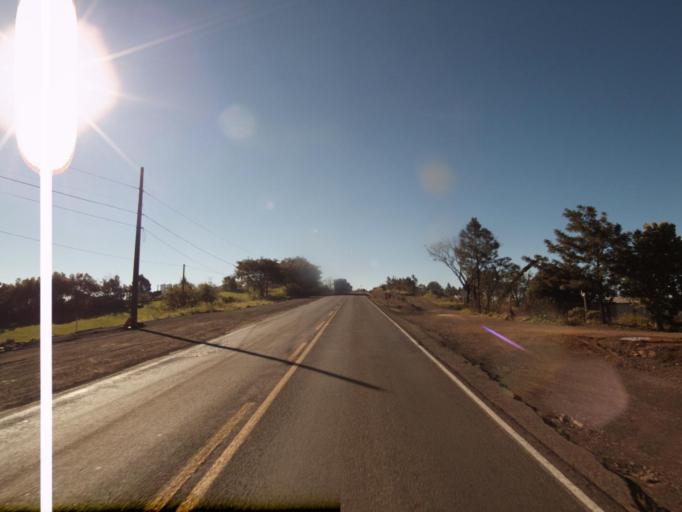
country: AR
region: Misiones
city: Bernardo de Irigoyen
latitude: -26.6835
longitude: -53.5146
